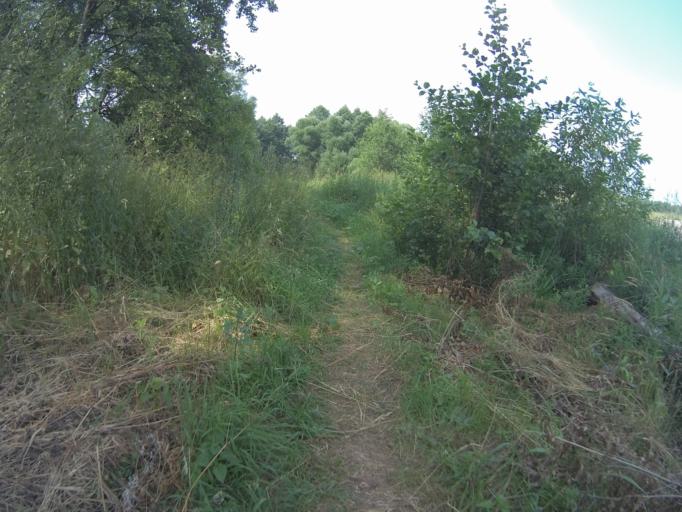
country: RU
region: Vladimir
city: Kommunar
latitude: 56.0724
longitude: 40.5573
